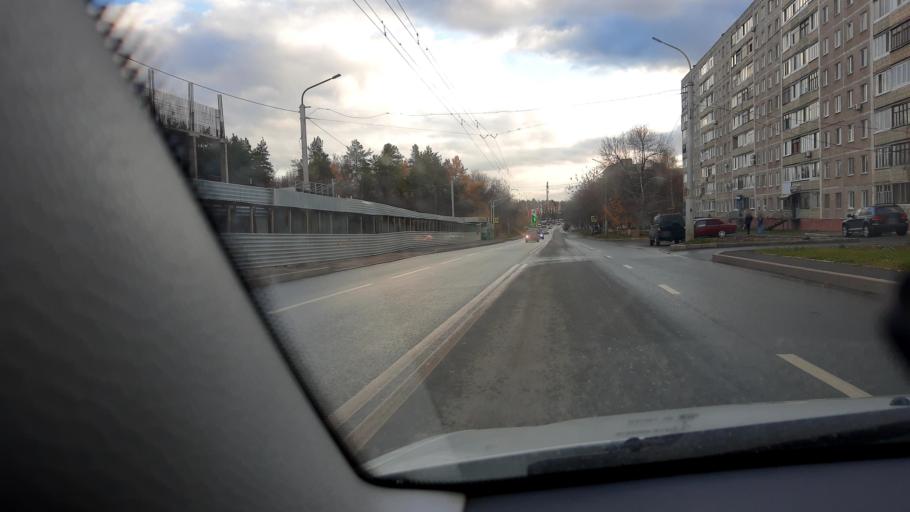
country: RU
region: Bashkortostan
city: Ufa
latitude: 54.7018
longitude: 56.0068
